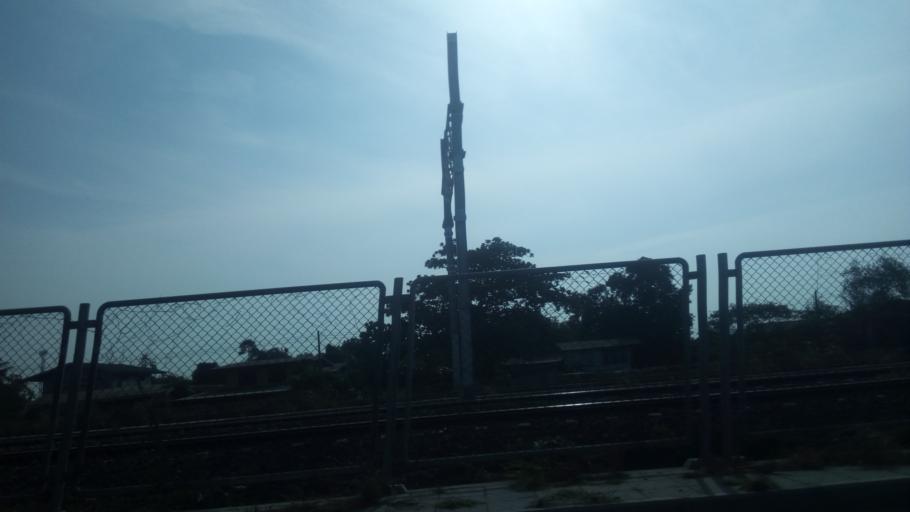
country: TH
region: Bangkok
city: Don Mueang
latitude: 13.9702
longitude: 100.6045
